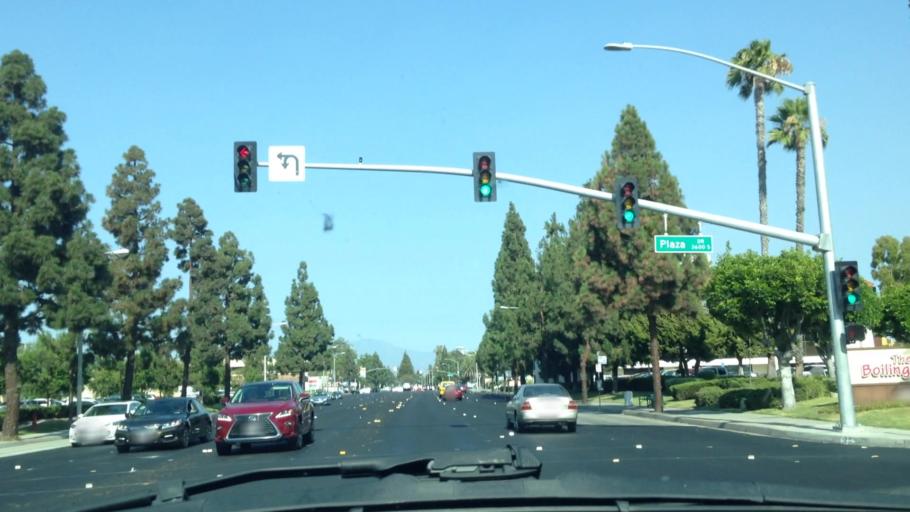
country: US
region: California
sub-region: Orange County
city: Santa Ana
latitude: 33.7000
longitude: -117.8889
